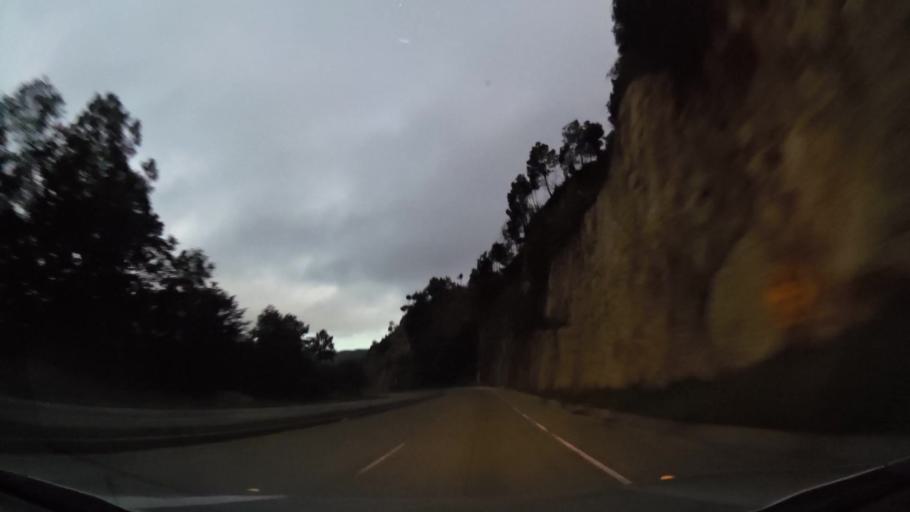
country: GT
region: Chimaltenango
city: Santa Apolonia
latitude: 14.8175
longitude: -90.9991
